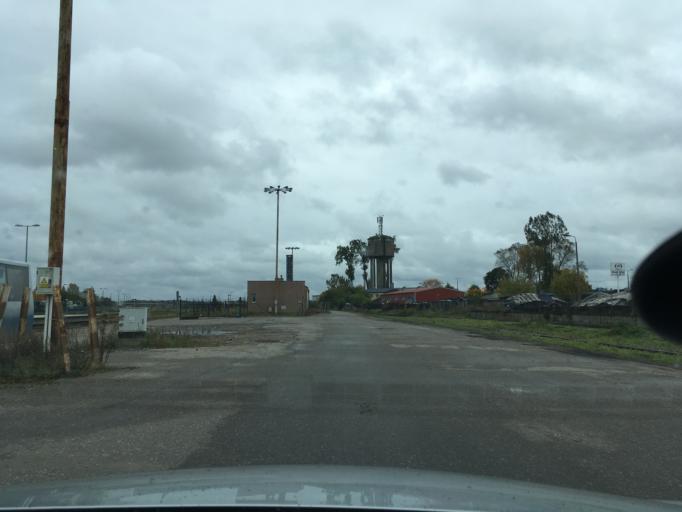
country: PL
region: Pomeranian Voivodeship
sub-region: Powiat koscierski
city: Koscierzyna
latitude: 54.1199
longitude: 17.9949
